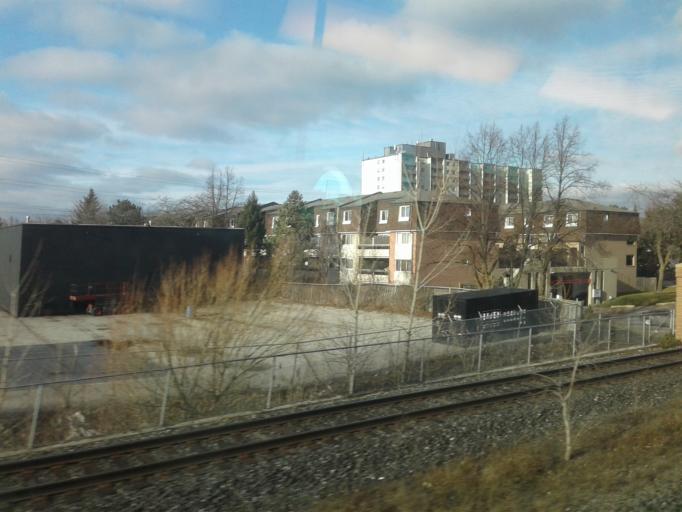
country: CA
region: Ontario
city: Mississauga
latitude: 43.5103
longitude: -79.6370
